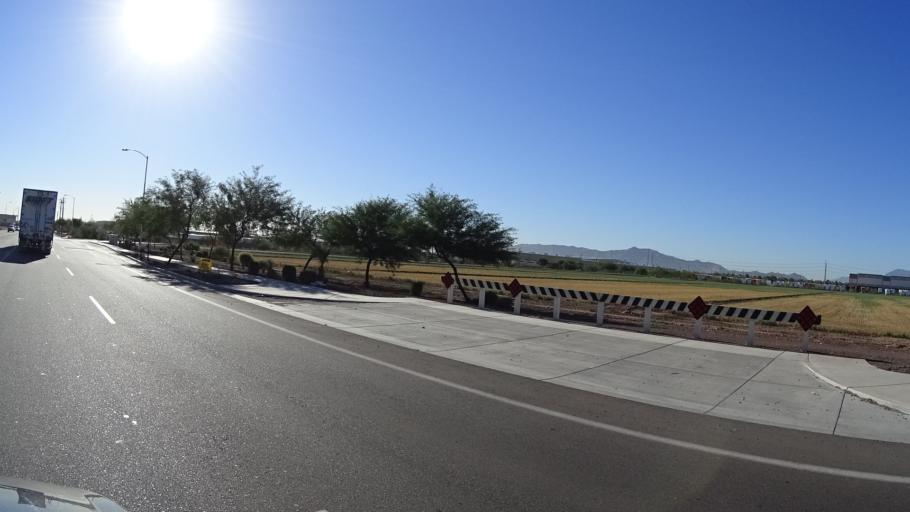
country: US
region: Arizona
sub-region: Maricopa County
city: Laveen
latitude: 33.4223
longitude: -112.1755
